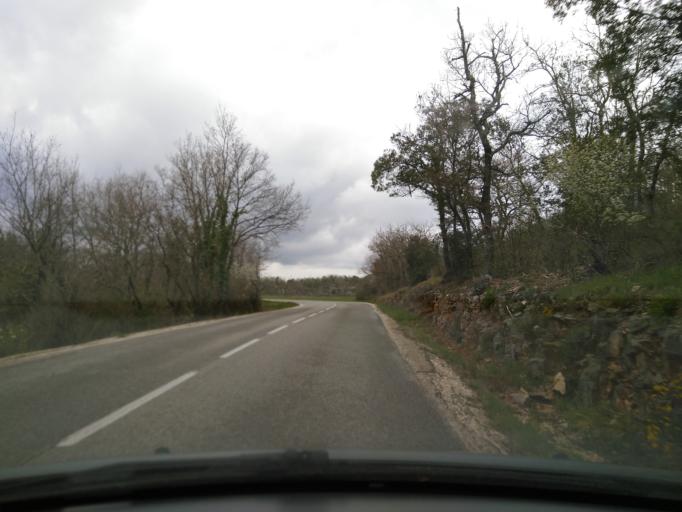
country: FR
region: Languedoc-Roussillon
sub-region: Departement du Gard
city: Barjac
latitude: 44.3575
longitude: 4.3760
